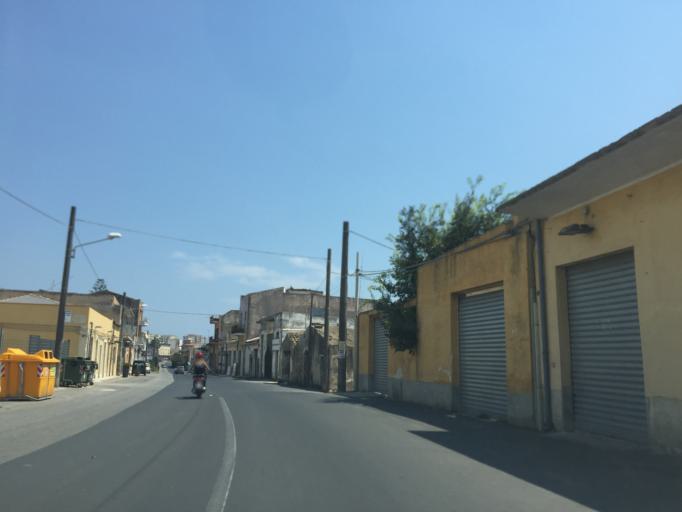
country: IT
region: Sicily
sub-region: Provincia di Siracusa
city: Siracusa
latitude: 37.0697
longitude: 15.2734
